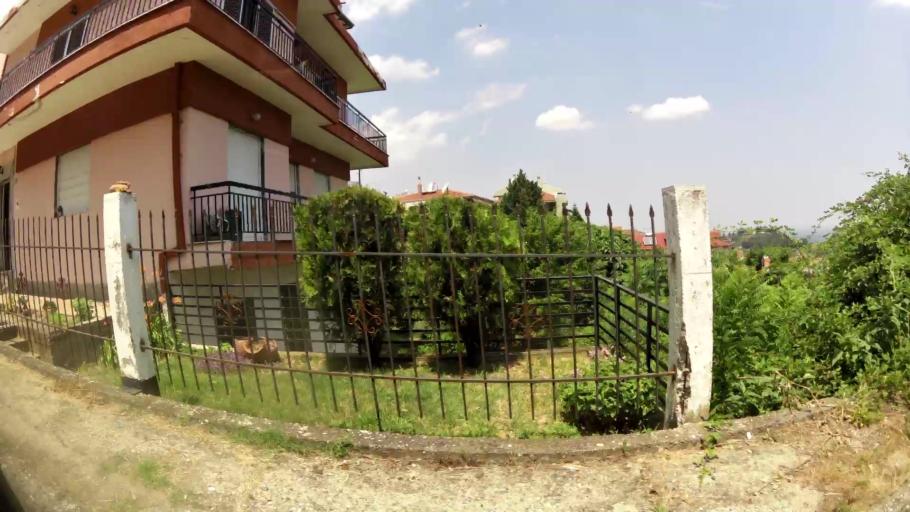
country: GR
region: Central Macedonia
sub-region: Nomos Imathias
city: Veroia
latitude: 40.5129
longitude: 22.1855
